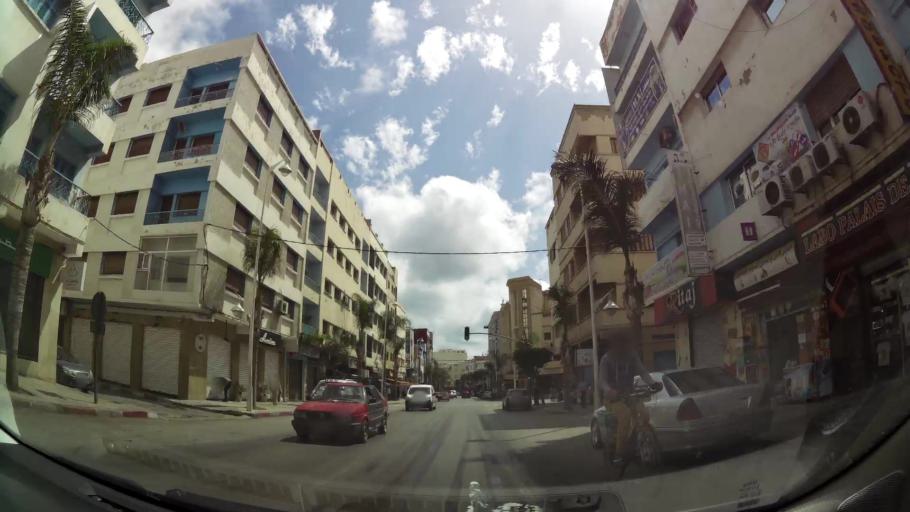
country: MA
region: Oriental
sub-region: Nador
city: Nador
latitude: 35.1704
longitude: -2.9320
